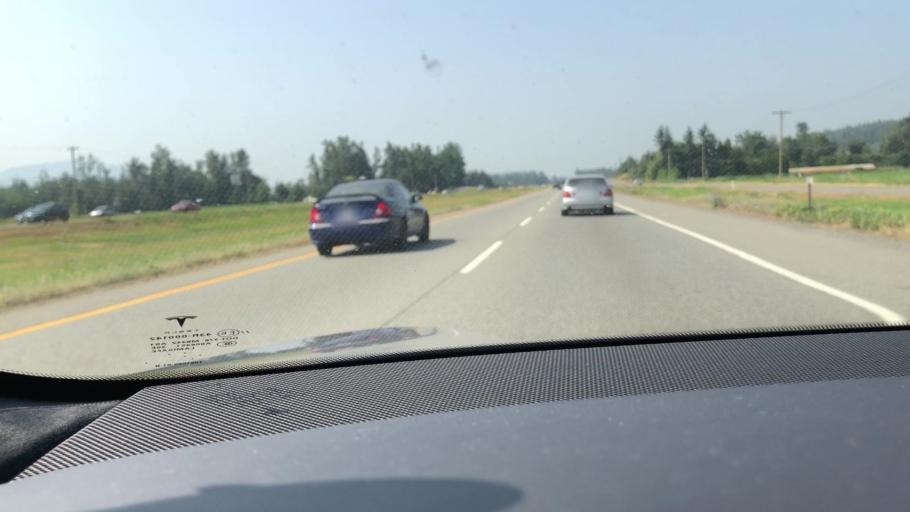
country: CA
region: British Columbia
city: Abbotsford
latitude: 49.0718
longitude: -122.1548
